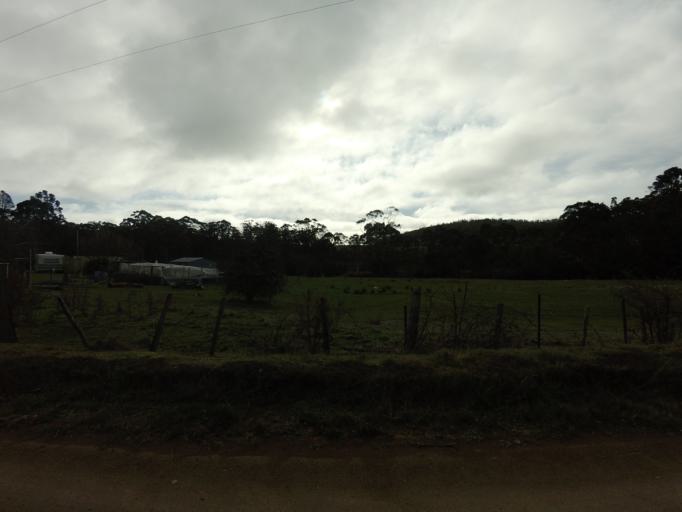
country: AU
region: Tasmania
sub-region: Derwent Valley
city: New Norfolk
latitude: -42.7545
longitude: 146.8770
